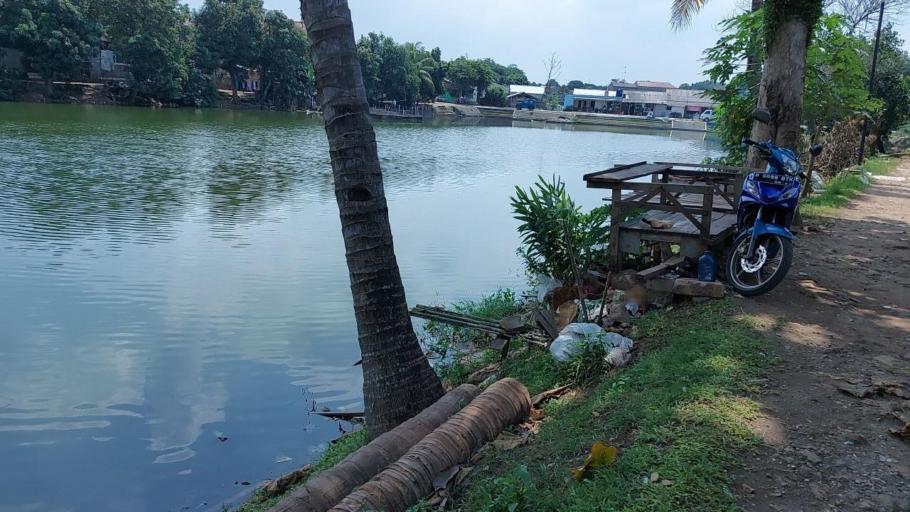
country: ID
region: West Java
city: Cibinong
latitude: -6.4713
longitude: 106.8476
